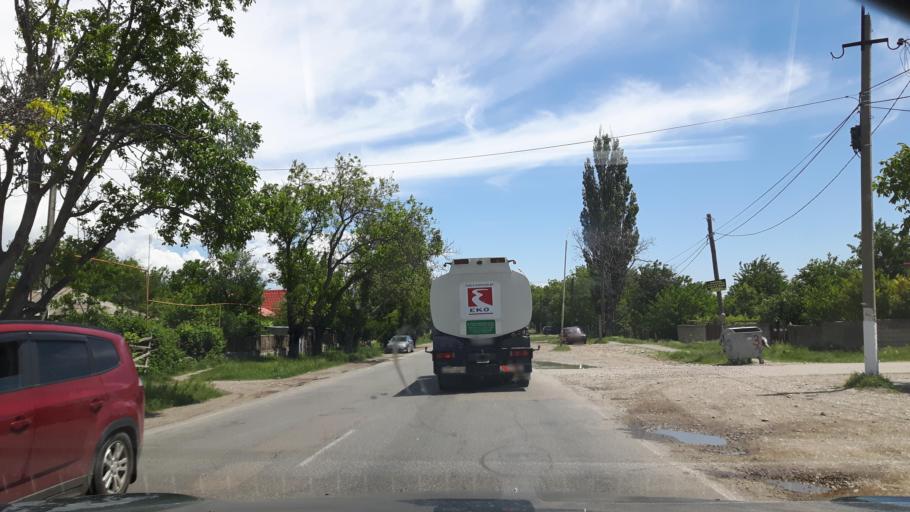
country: GE
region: Kakheti
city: Sagarejo
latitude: 41.7148
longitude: 45.1667
